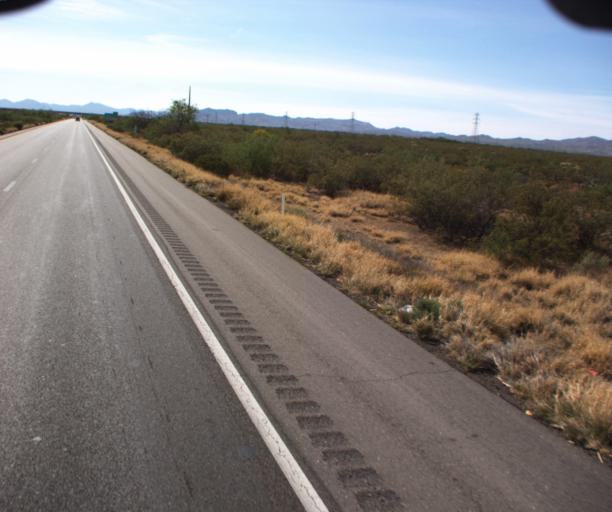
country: US
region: Arizona
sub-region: Pima County
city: Vail
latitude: 32.0313
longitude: -110.7270
